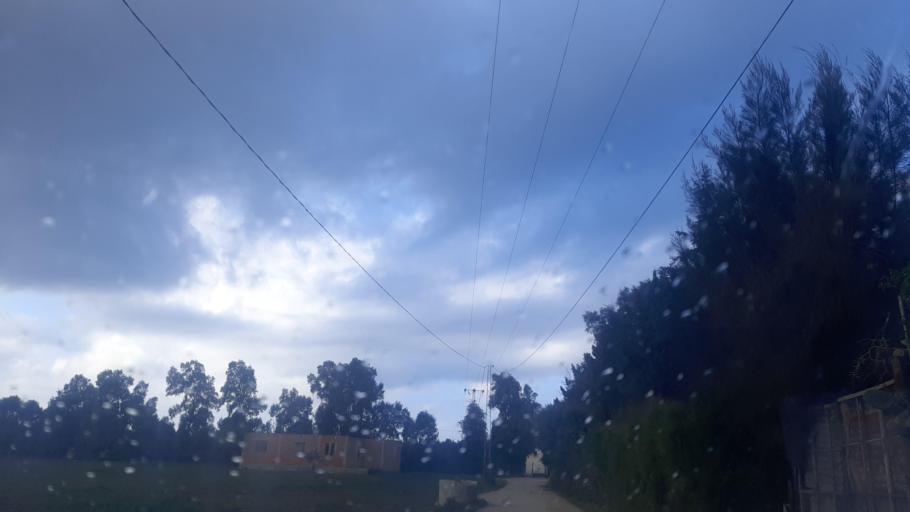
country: TN
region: Nabul
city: Manzil Bu Zalafah
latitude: 36.7398
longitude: 10.5300
